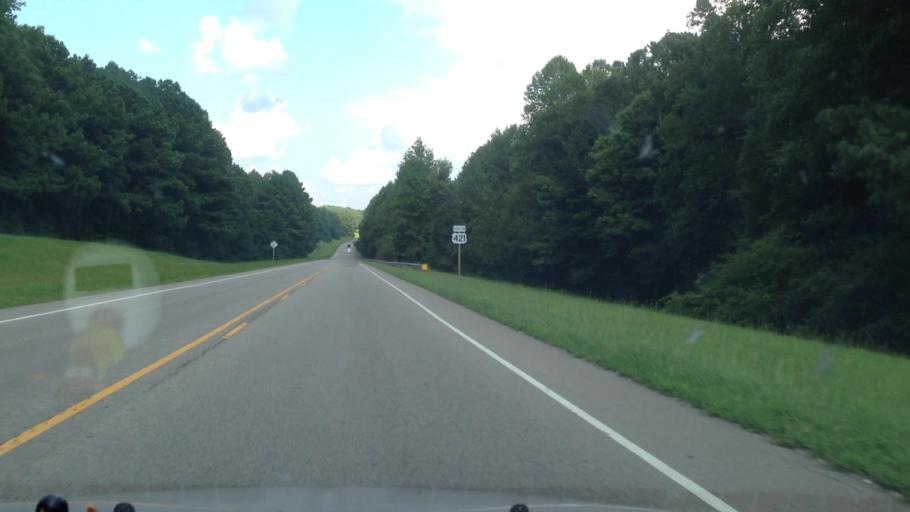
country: US
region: North Carolina
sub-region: Lee County
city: Broadway
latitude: 35.4397
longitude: -79.0849
